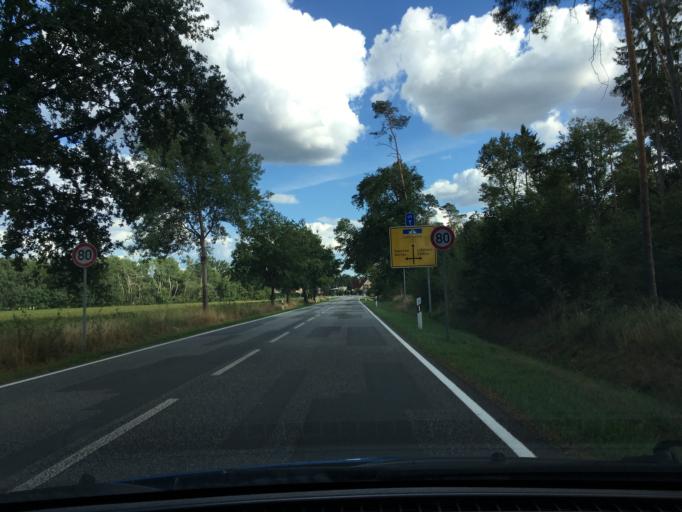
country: DE
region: Mecklenburg-Vorpommern
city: Lubtheen
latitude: 53.3583
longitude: 11.1403
